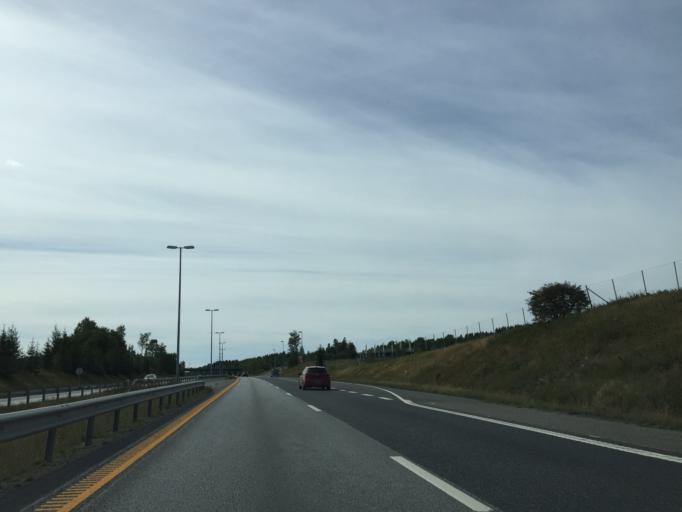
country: NO
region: Akershus
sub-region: Vestby
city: Vestby
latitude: 59.6291
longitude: 10.7360
